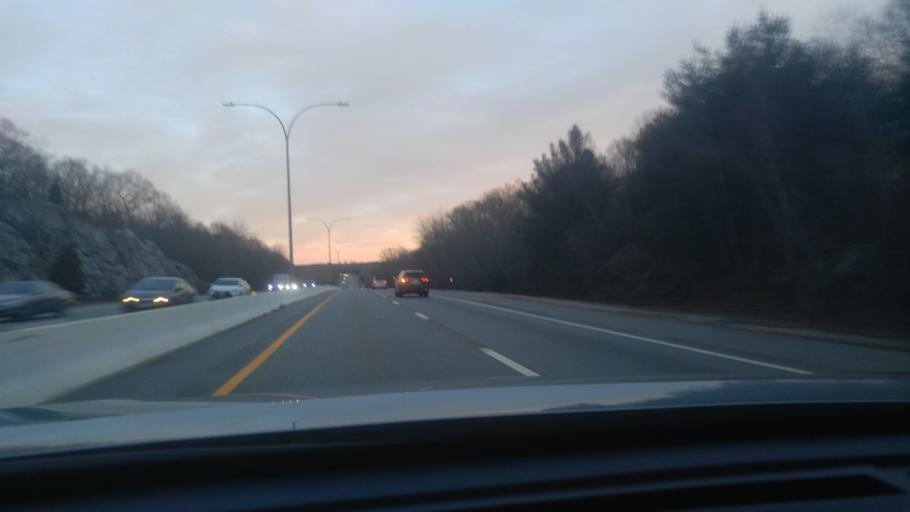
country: US
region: Rhode Island
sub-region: Washington County
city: North Kingstown
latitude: 41.5306
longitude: -71.4522
